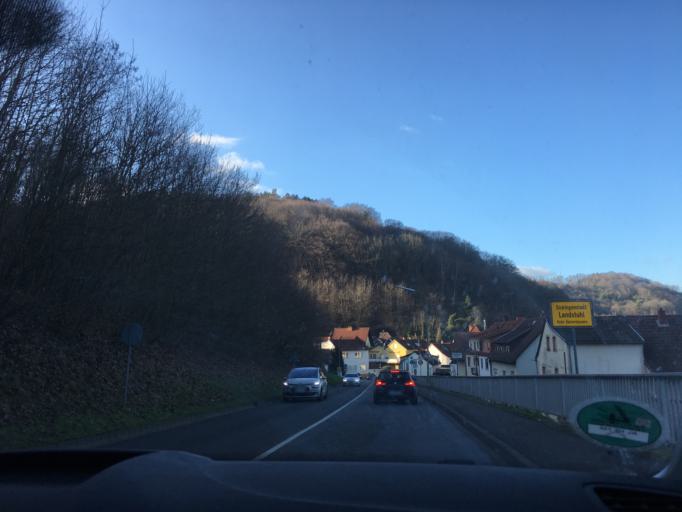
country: DE
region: Rheinland-Pfalz
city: Landstuhl
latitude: 49.4049
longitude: 7.5725
